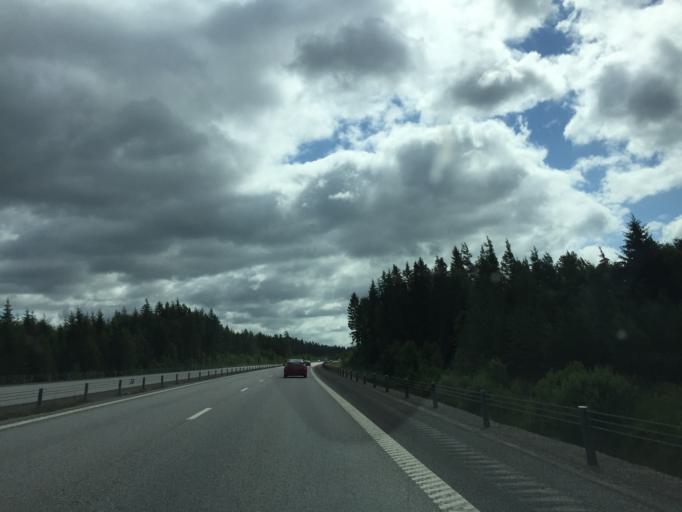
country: SE
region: OErebro
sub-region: Orebro Kommun
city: Orebro
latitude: 59.2466
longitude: 15.0825
